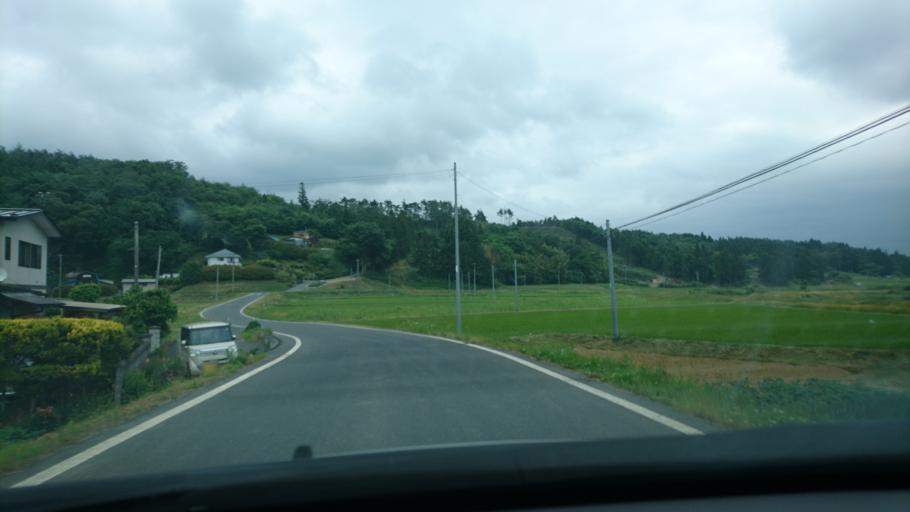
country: JP
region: Iwate
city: Ichinoseki
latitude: 38.9279
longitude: 141.1737
